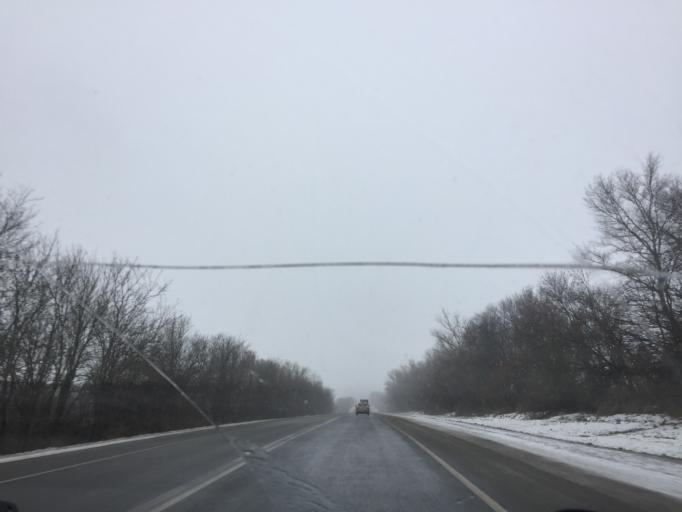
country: RU
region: Tula
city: Plavsk
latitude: 53.7982
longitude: 37.3771
